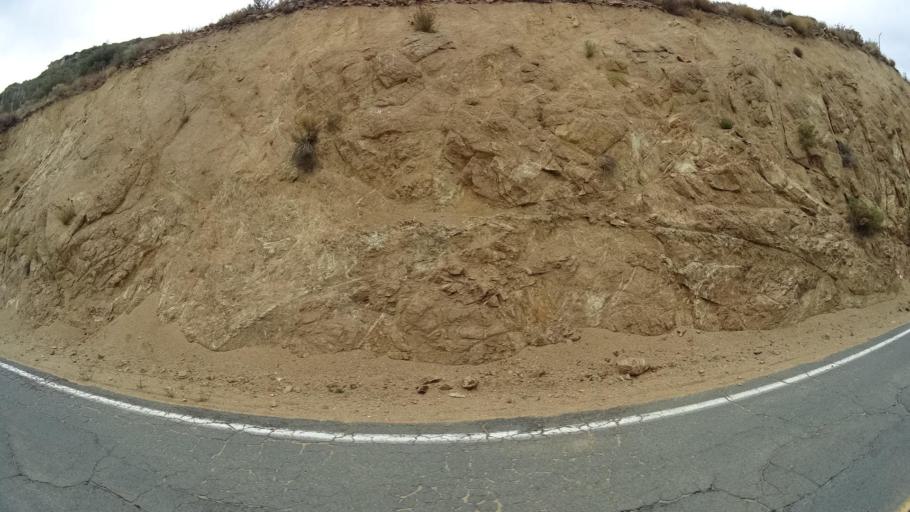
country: US
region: California
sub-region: San Diego County
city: Pine Valley
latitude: 32.7610
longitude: -116.4520
